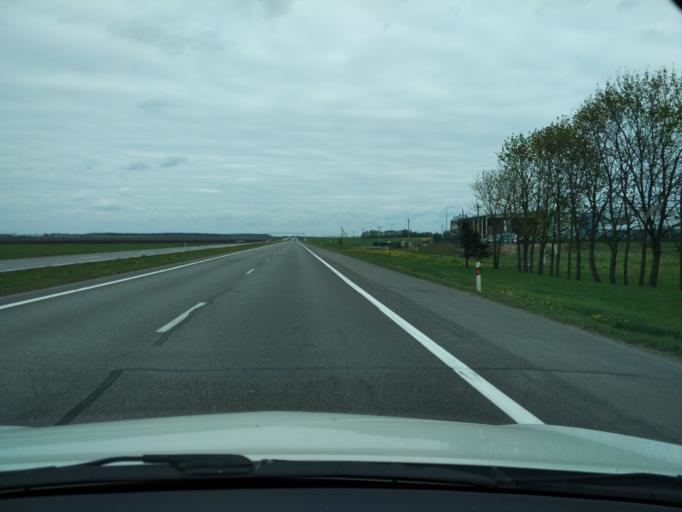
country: BY
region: Minsk
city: Machulishchy
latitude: 53.7353
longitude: 27.5678
